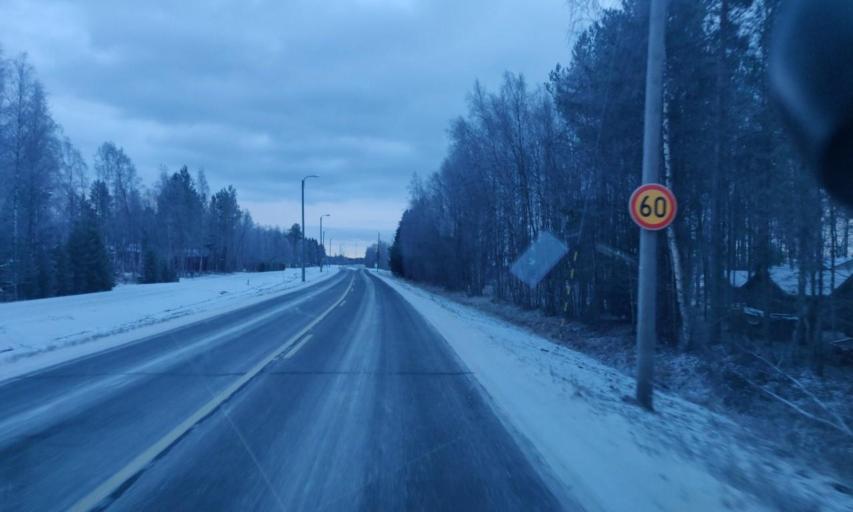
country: FI
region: Northern Ostrobothnia
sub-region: Oulu
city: Oulunsalo
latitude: 64.9869
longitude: 25.2606
